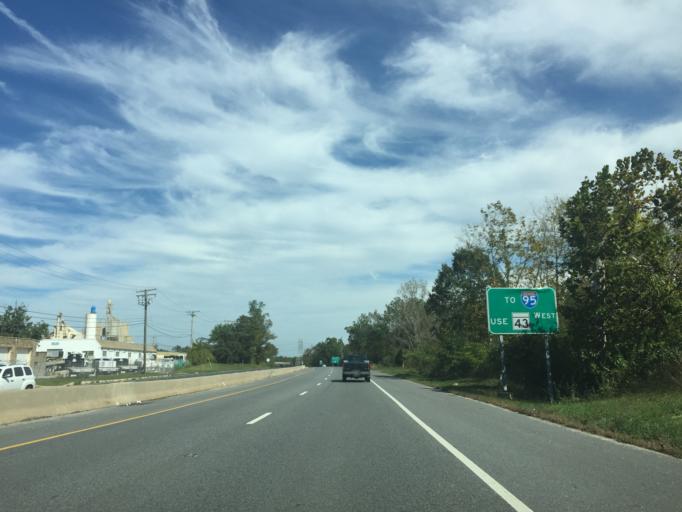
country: US
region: Maryland
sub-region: Baltimore County
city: White Marsh
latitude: 39.3677
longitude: -76.4377
